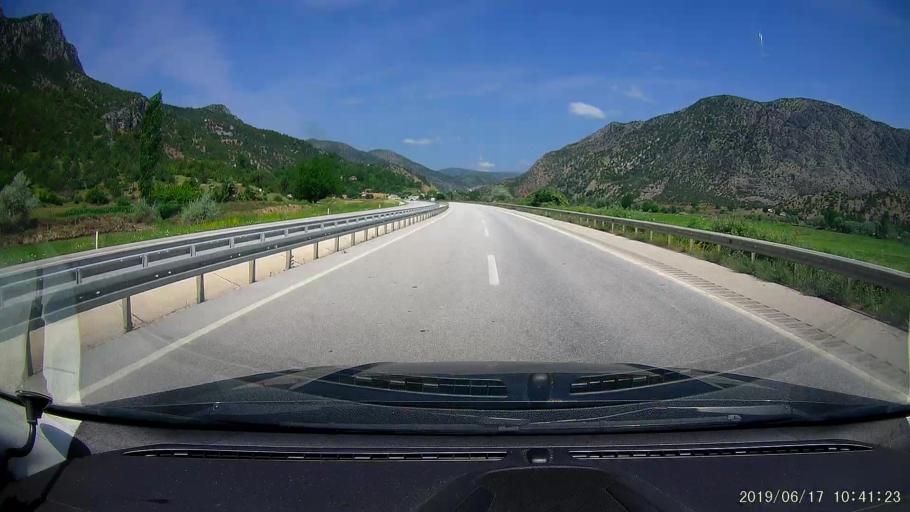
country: TR
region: Corum
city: Kargi
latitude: 41.0391
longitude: 34.5779
